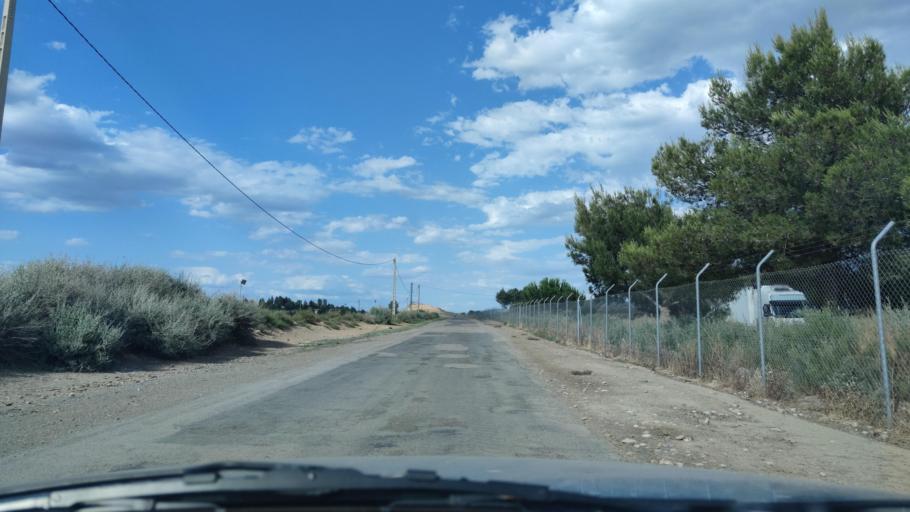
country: ES
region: Catalonia
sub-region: Provincia de Lleida
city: Alcarras
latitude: 41.6060
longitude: 0.5359
